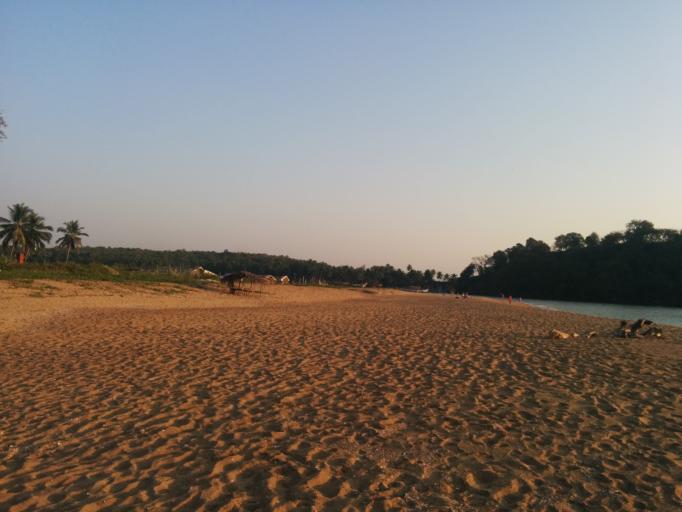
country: IN
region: Karnataka
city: Canacona
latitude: 14.9869
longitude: 74.0379
